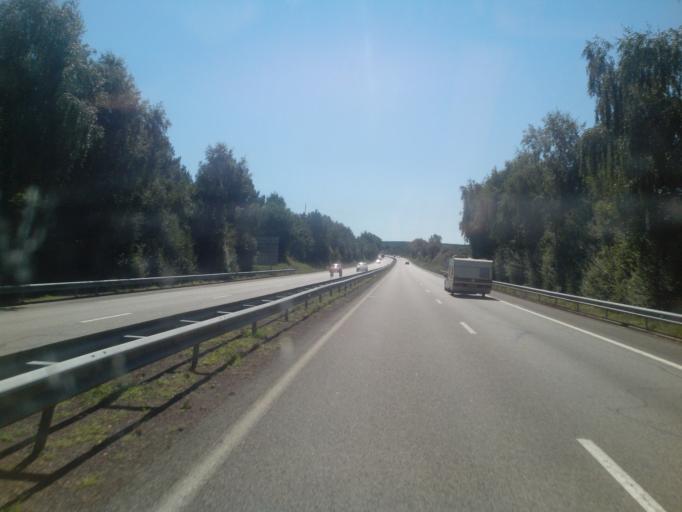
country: FR
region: Brittany
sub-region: Departement du Morbihan
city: Malestroit
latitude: 47.8322
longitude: -2.4307
